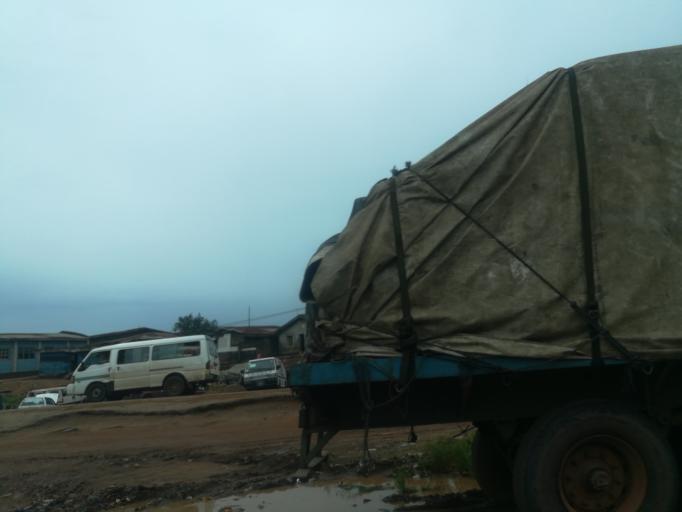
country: NG
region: Oyo
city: Ibadan
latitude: 7.3681
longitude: 3.9288
